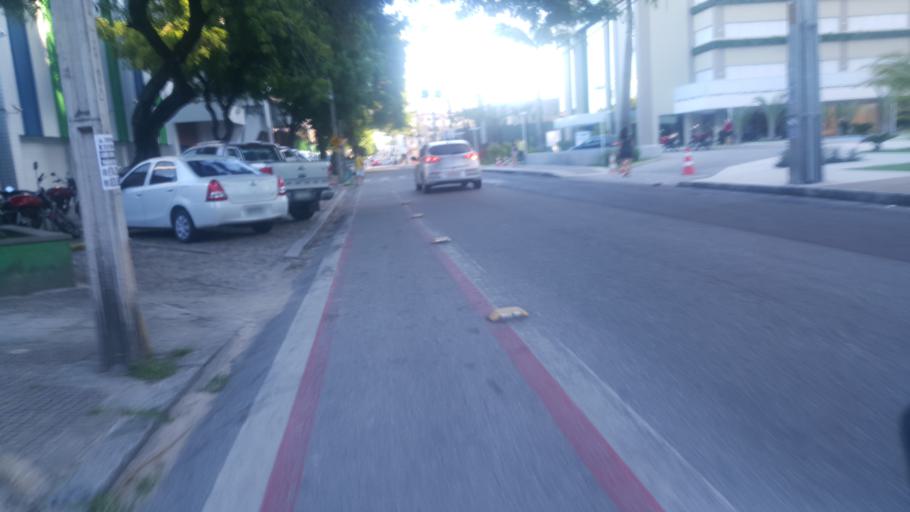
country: BR
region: Ceara
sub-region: Fortaleza
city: Fortaleza
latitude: -3.7412
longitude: -38.5339
